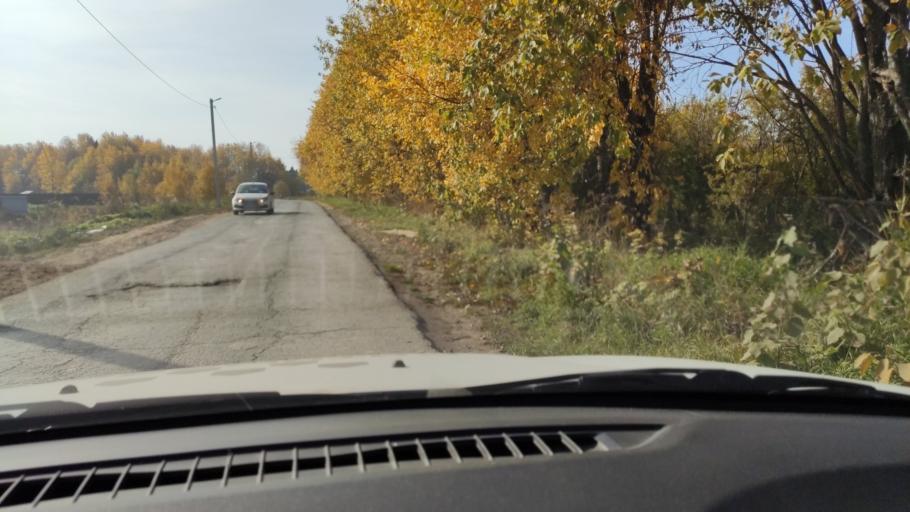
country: RU
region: Perm
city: Sylva
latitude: 58.0366
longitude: 56.7414
